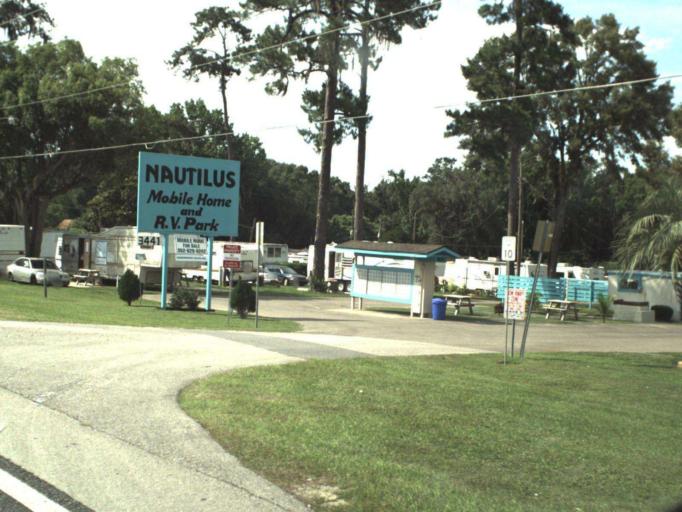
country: US
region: Florida
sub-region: Marion County
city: Ocala
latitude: 29.1536
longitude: -82.1246
